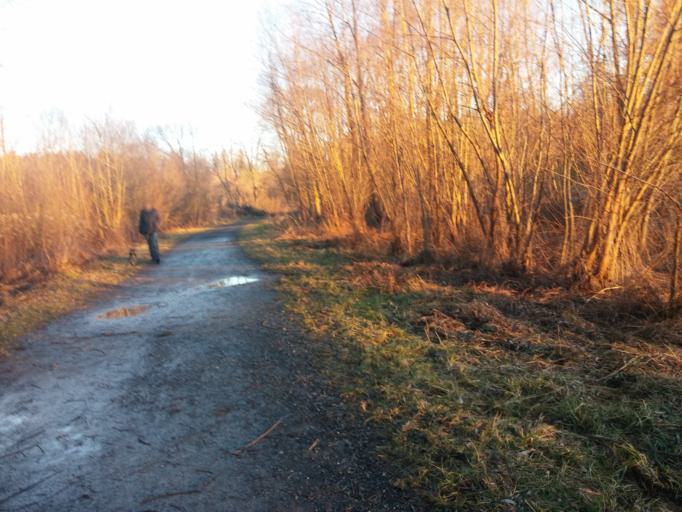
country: DE
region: Bavaria
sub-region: Swabia
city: Dietmannsried
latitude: 47.7973
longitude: 10.2844
